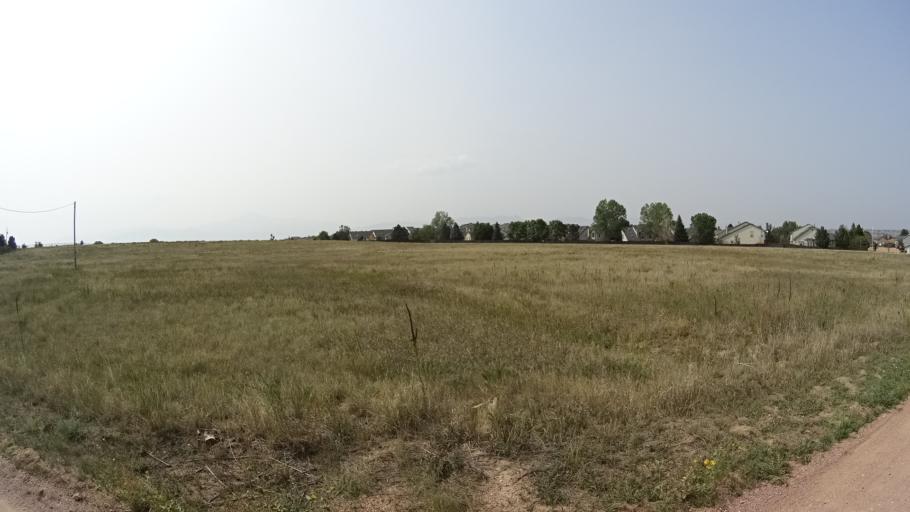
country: US
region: Colorado
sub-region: El Paso County
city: Cimarron Hills
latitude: 38.9148
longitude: -104.7289
